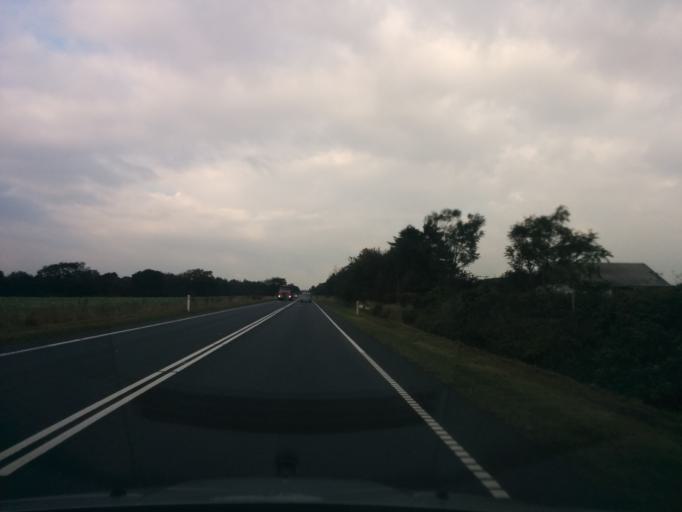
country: DK
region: South Denmark
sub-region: Esbjerg Kommune
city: Bramming
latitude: 55.6166
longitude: 8.7534
